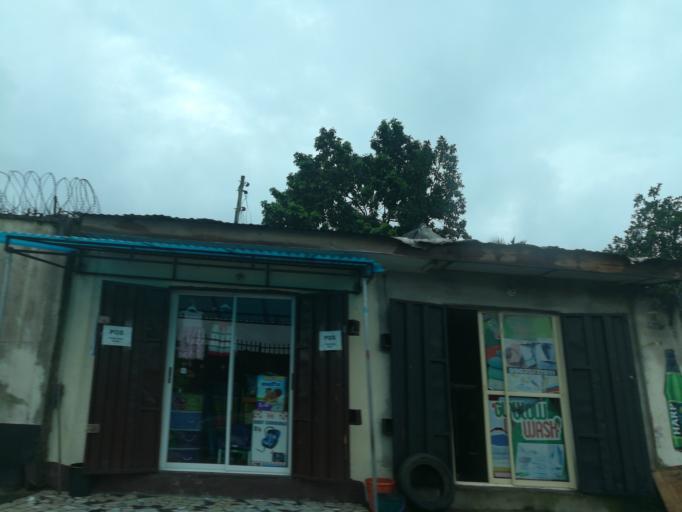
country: NG
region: Rivers
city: Port Harcourt
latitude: 4.8582
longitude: 7.0326
